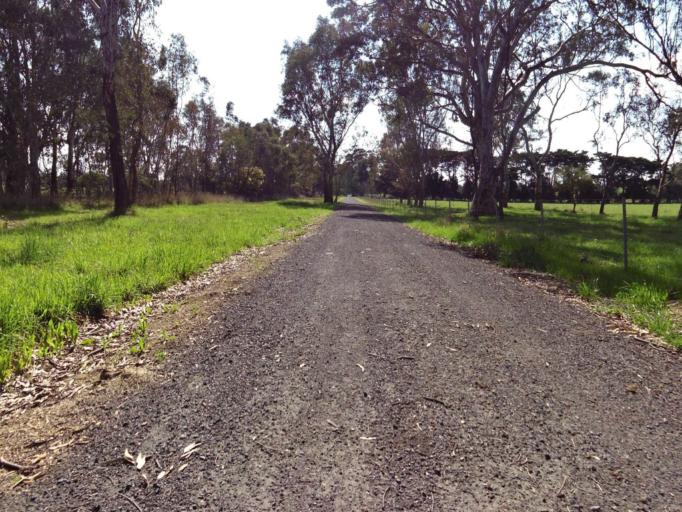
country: AU
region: Victoria
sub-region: Murrindindi
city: Alexandra
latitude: -37.1256
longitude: 145.5985
